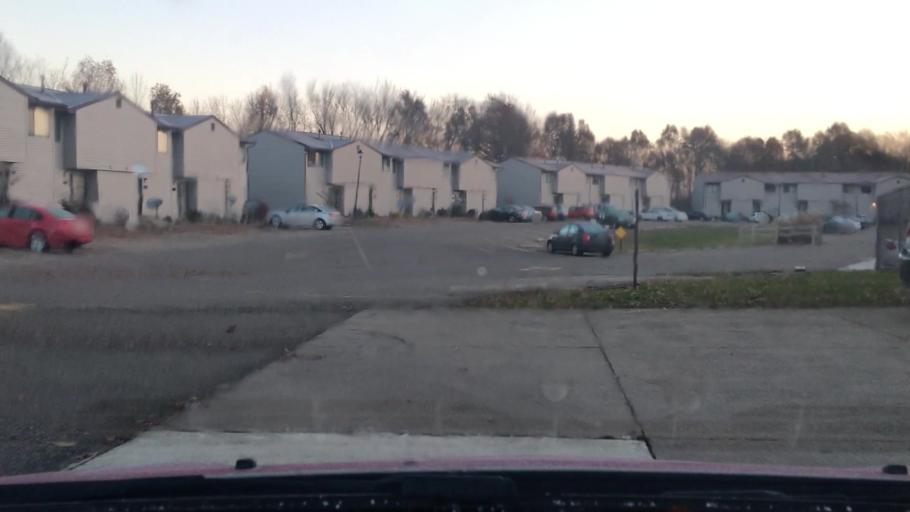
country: US
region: Ohio
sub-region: Wayne County
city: Wooster
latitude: 40.7884
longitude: -81.9270
